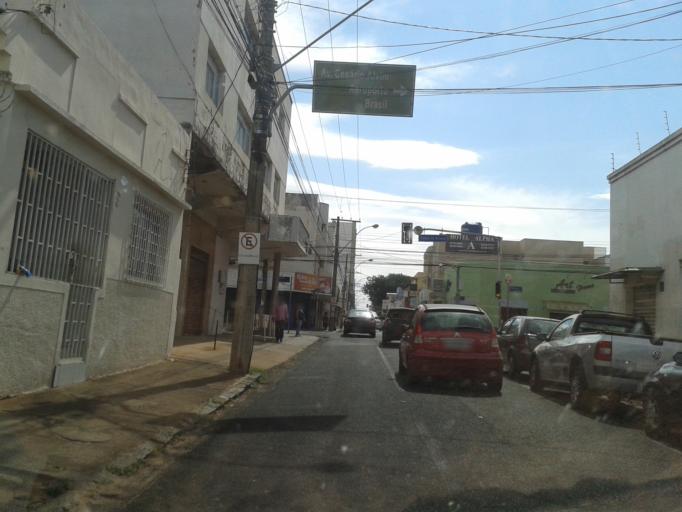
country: BR
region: Minas Gerais
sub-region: Uberlandia
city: Uberlandia
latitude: -18.9179
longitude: -48.2732
